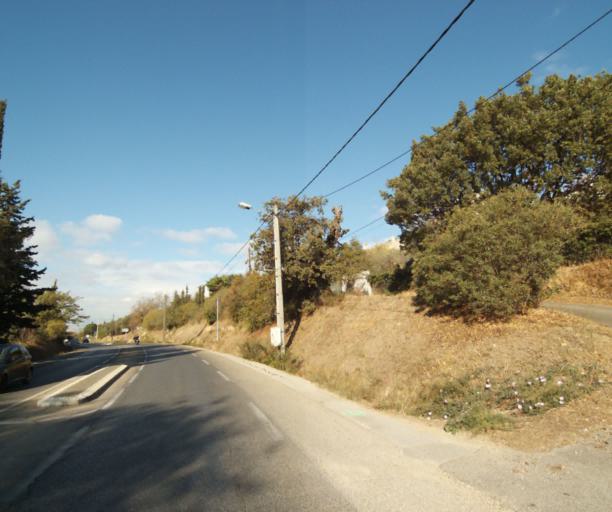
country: FR
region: Provence-Alpes-Cote d'Azur
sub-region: Departement des Bouches-du-Rhone
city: Allauch
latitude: 43.3334
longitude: 5.4828
